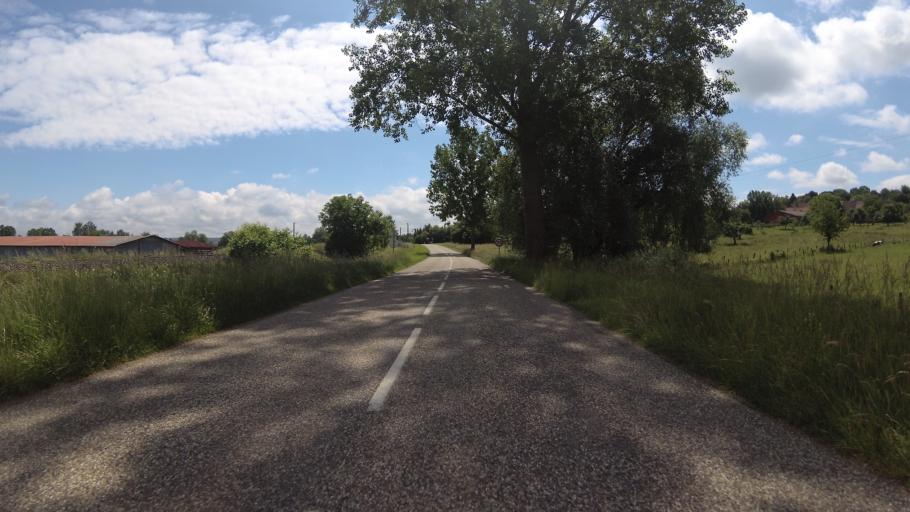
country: FR
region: Alsace
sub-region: Departement du Bas-Rhin
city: Diemeringen
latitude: 48.9548
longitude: 7.1505
